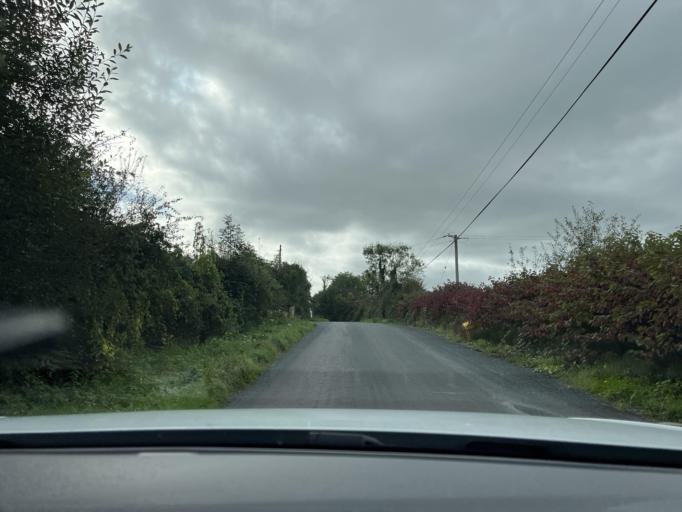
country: IE
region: Connaught
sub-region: County Leitrim
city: Carrick-on-Shannon
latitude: 53.9672
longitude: -8.0827
